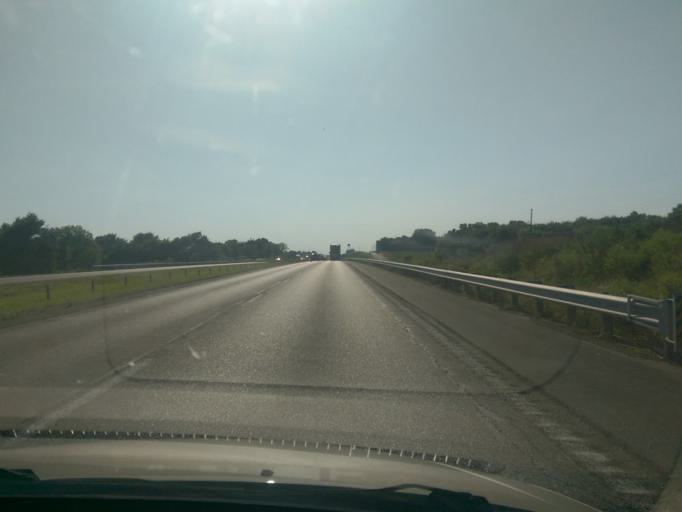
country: US
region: Missouri
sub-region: Lafayette County
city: Higginsville
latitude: 39.0023
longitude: -93.7972
